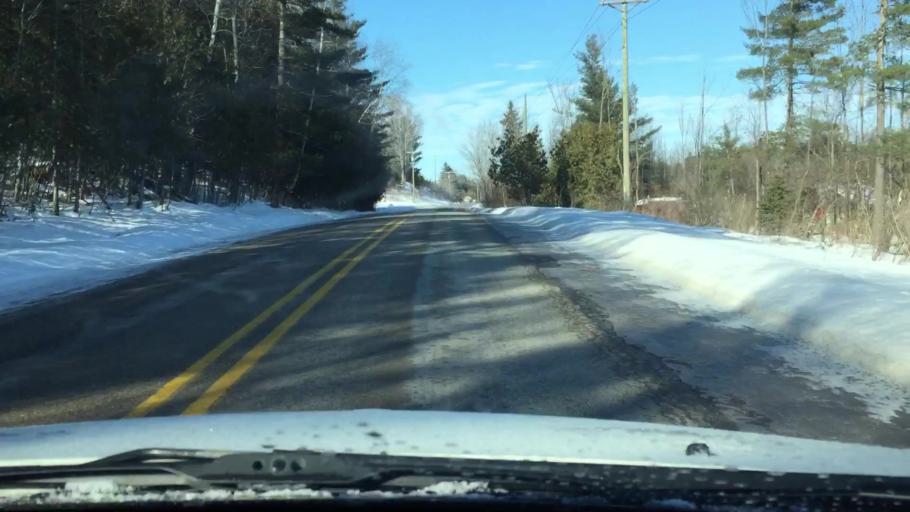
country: US
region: Michigan
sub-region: Charlevoix County
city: East Jordan
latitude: 45.1086
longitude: -85.1289
